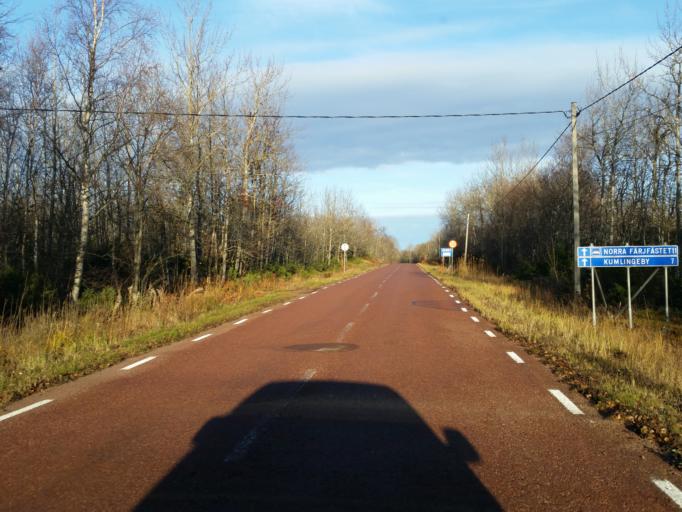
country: AX
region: Alands skaergard
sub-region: Kumlinge
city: Kumlinge
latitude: 60.2206
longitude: 20.7287
